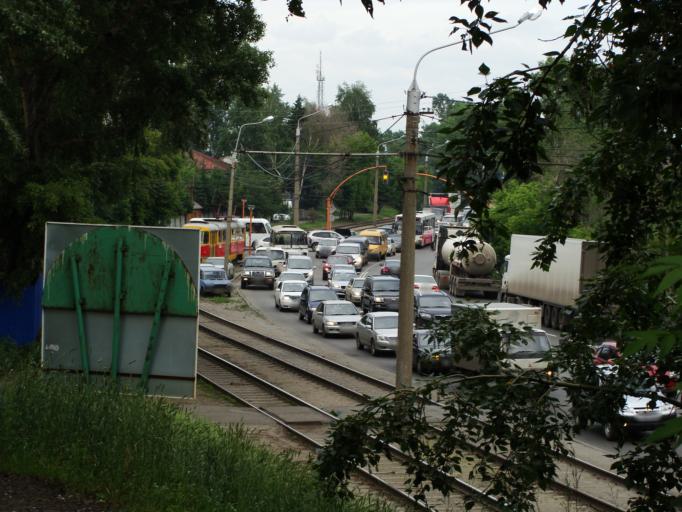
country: RU
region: Altai Krai
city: Zaton
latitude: 53.3068
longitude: 83.7705
